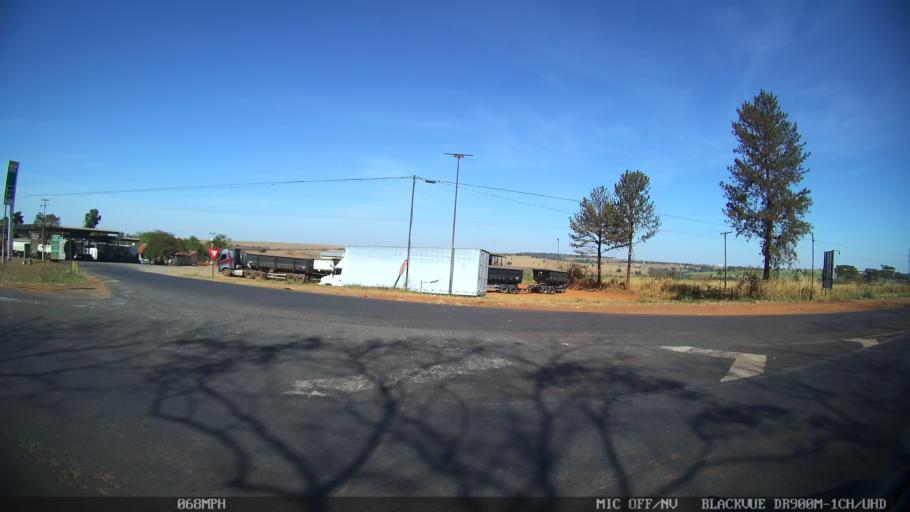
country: BR
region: Sao Paulo
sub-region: Barretos
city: Barretos
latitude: -20.5010
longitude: -48.5412
